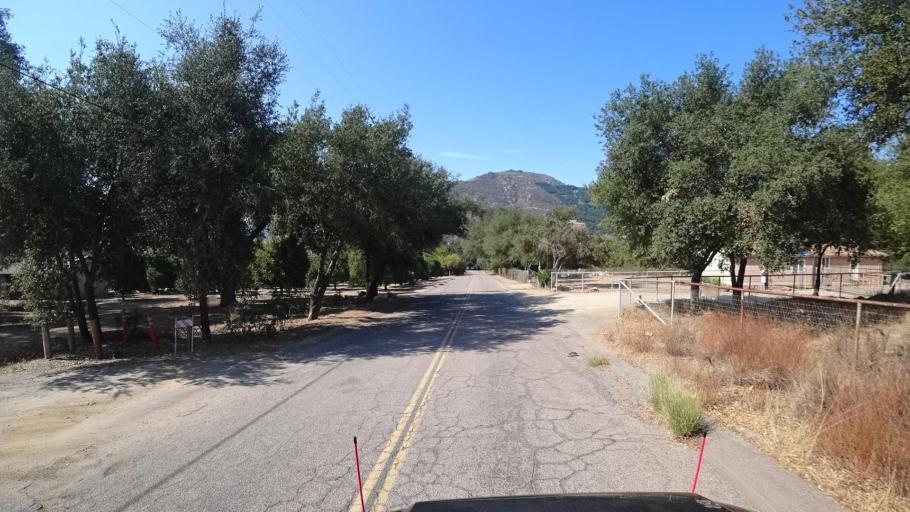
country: US
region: California
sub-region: San Diego County
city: Valley Center
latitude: 33.3423
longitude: -117.0107
